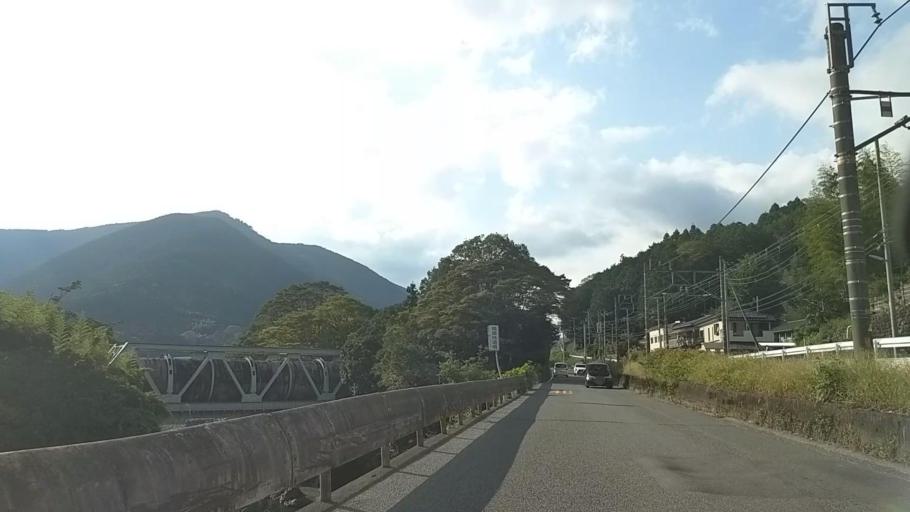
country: JP
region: Shizuoka
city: Fujinomiya
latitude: 35.2009
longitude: 138.5581
